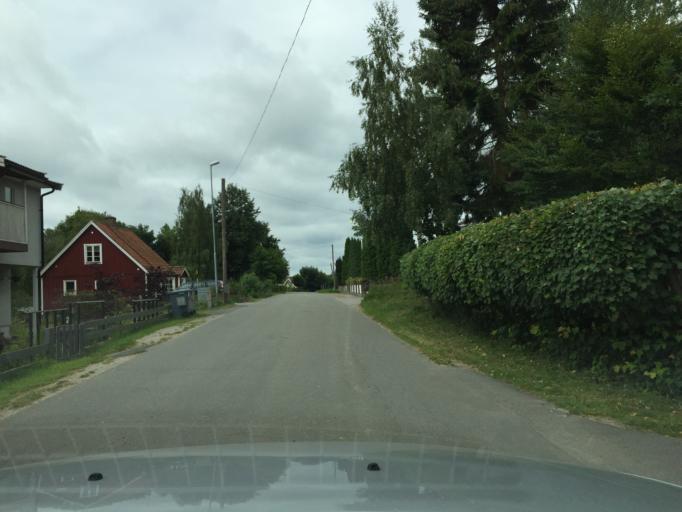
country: SE
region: Skane
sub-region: Hassleholms Kommun
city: Sosdala
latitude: 56.0311
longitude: 13.6693
